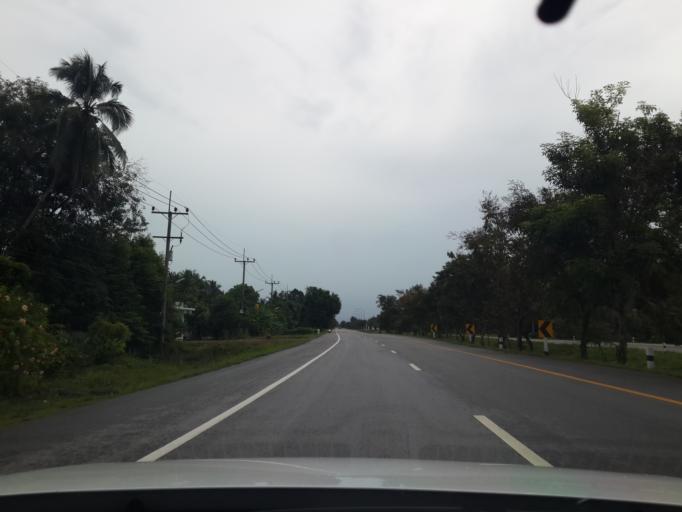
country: TH
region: Pattani
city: Khok Pho
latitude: 6.8145
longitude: 101.0888
